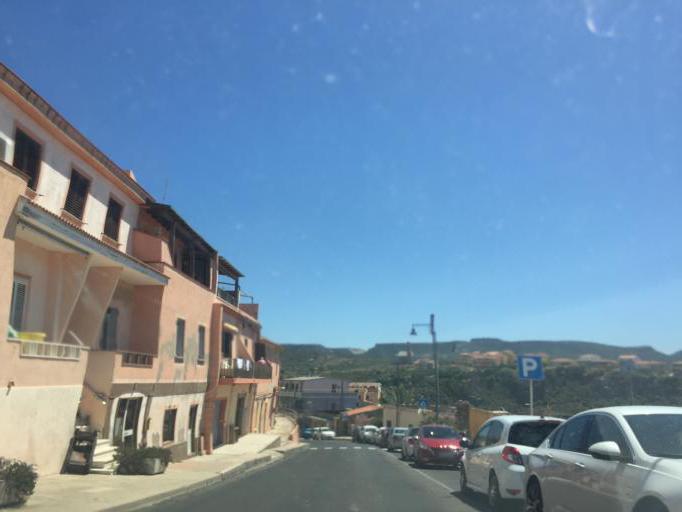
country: IT
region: Sardinia
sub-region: Provincia di Sassari
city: Castelsardo
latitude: 40.9157
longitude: 8.7111
